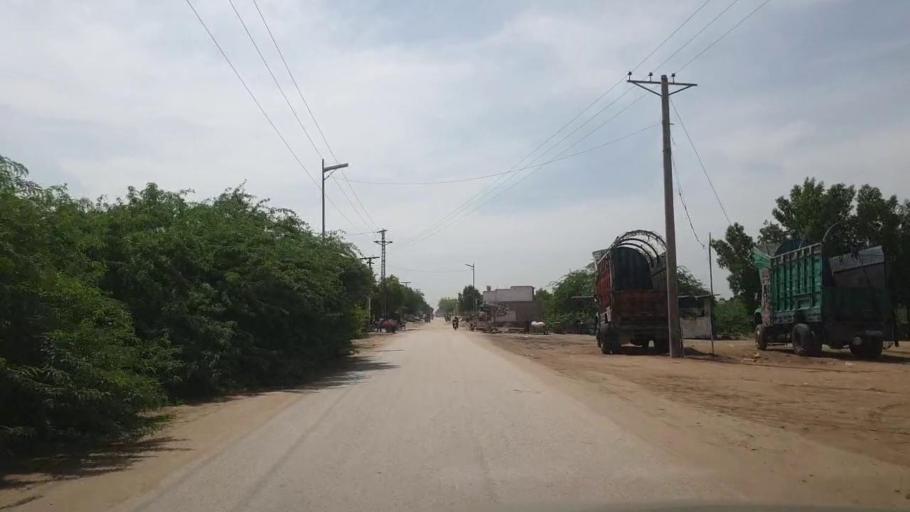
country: PK
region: Sindh
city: Kot Diji
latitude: 27.1593
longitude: 68.9584
